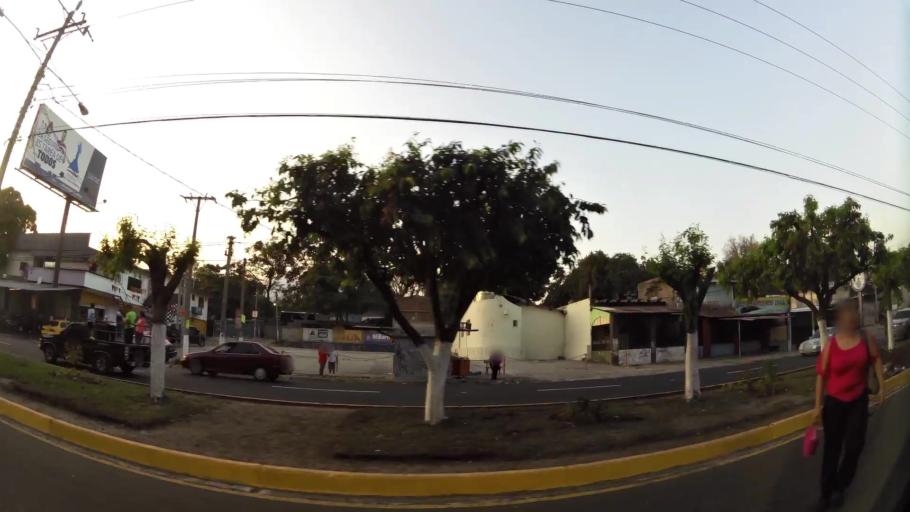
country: SV
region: San Salvador
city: Mejicanos
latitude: 13.7143
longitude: -89.2044
